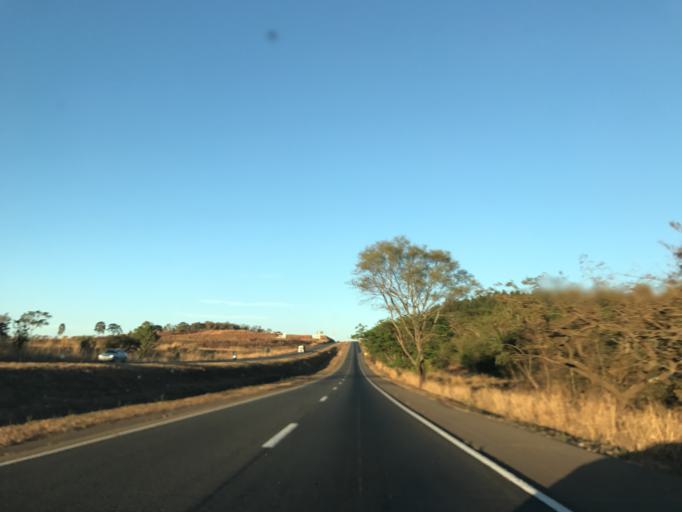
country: BR
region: Goias
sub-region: Anapolis
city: Anapolis
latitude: -16.3259
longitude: -48.8809
